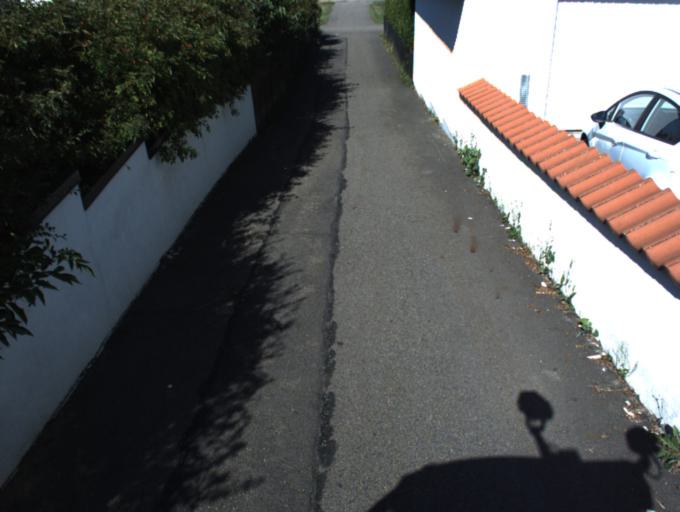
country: SE
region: Skane
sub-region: Helsingborg
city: Helsingborg
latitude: 56.0934
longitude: 12.6506
